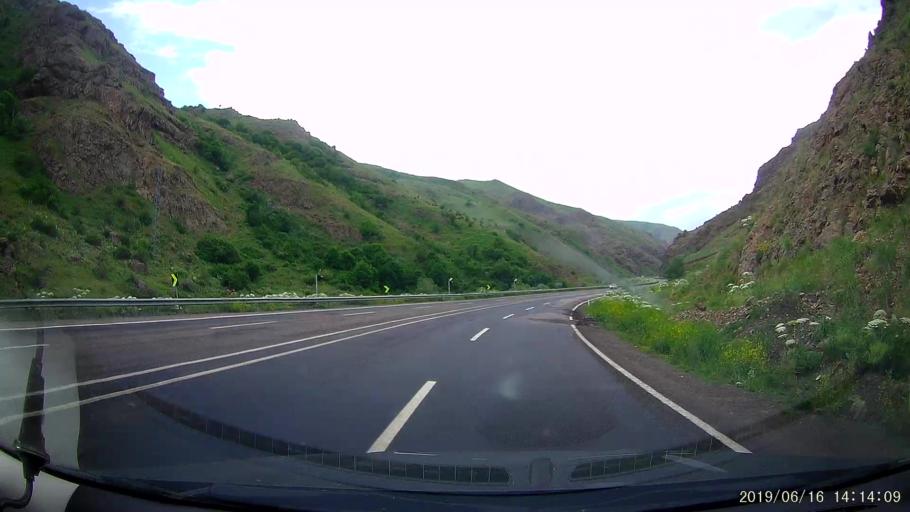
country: TR
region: Agri
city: Tahir
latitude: 39.7946
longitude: 42.5034
